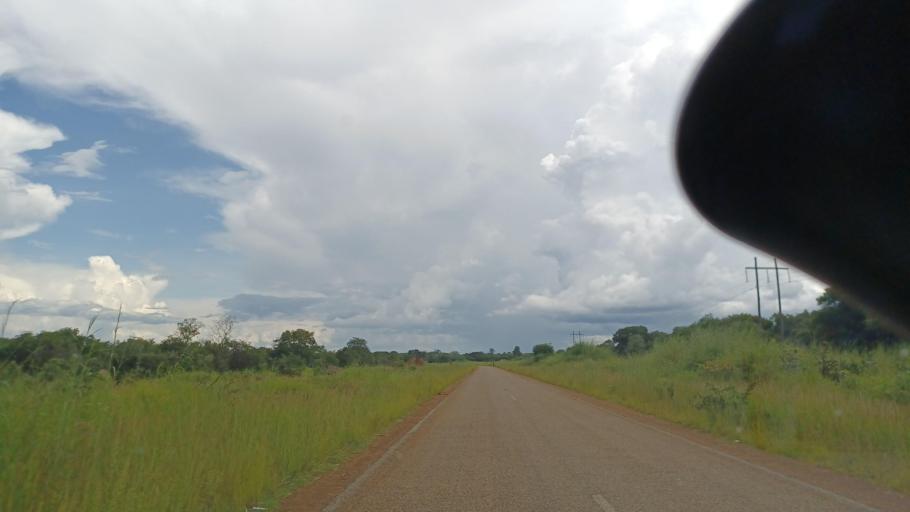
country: ZM
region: North-Western
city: Kasempa
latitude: -13.1192
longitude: 25.8702
